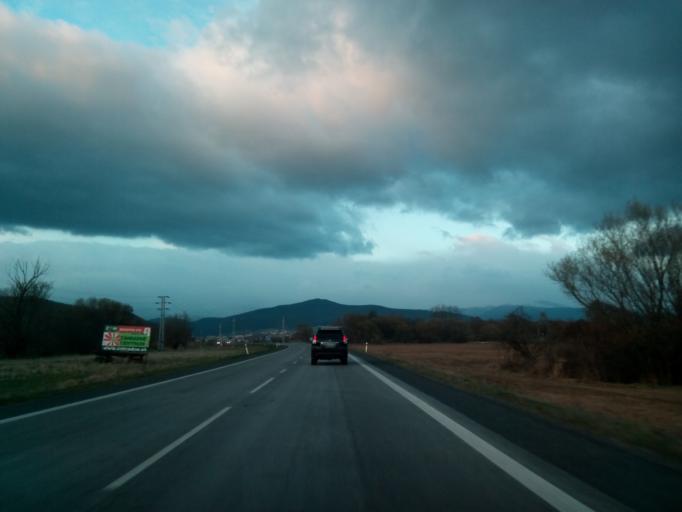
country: SK
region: Kosicky
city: Roznava
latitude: 48.6255
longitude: 20.4996
